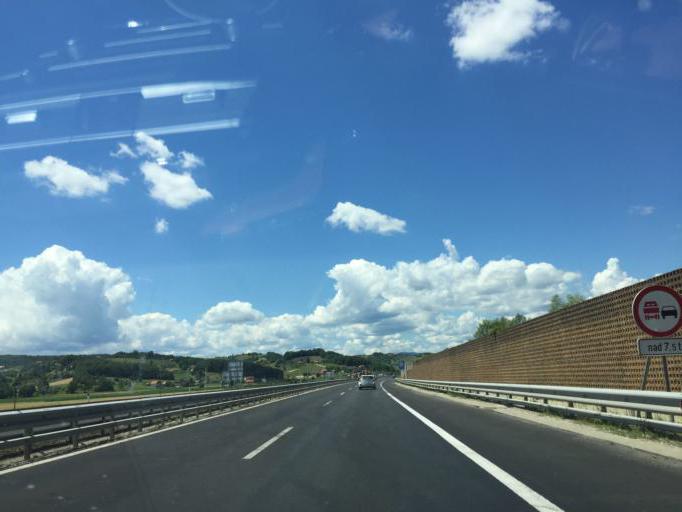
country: SI
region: Sveti Jurij v Slovenskih Goricah
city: Jurovski Dol
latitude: 46.5753
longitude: 15.7462
